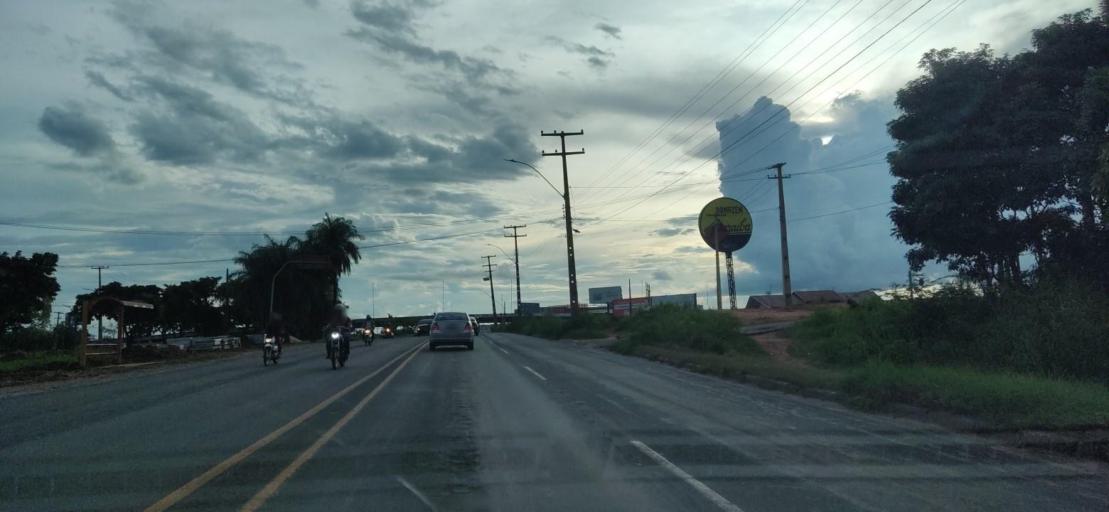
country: BR
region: Piaui
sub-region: Teresina
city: Teresina
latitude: -5.1220
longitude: -42.7935
